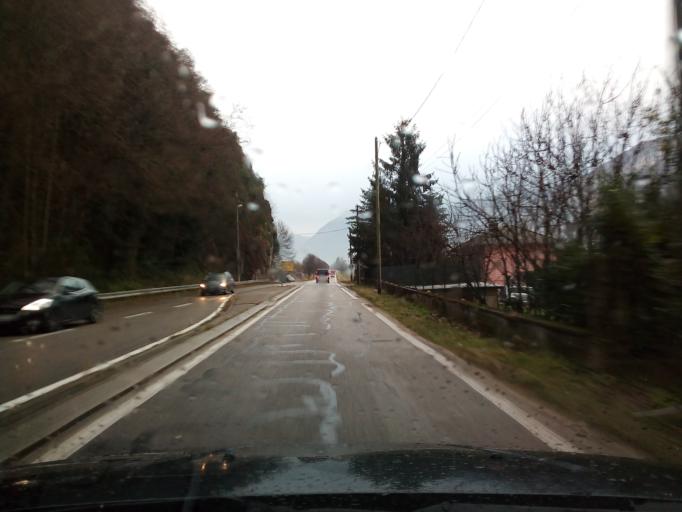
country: FR
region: Rhone-Alpes
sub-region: Departement de l'Isere
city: La Buisse
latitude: 45.3169
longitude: 5.6220
